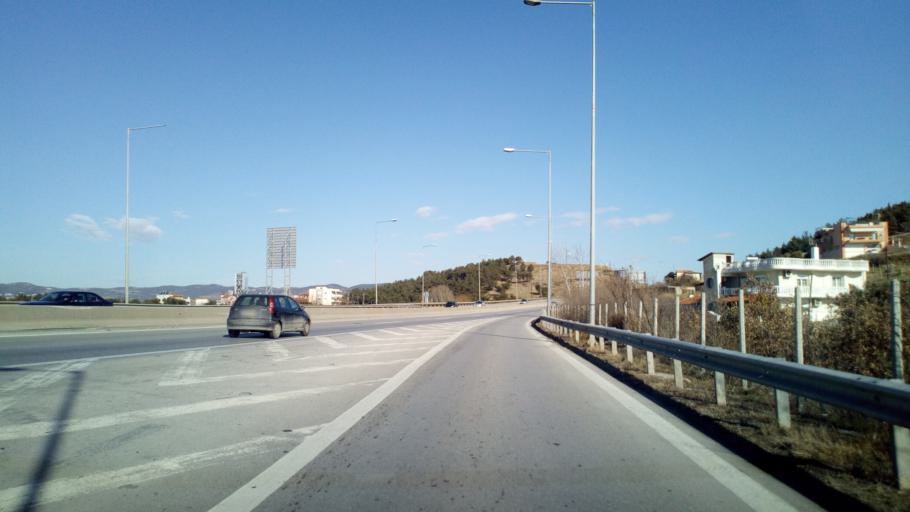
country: GR
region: Central Macedonia
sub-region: Nomos Thessalonikis
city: Efkarpia
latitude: 40.6835
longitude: 22.9574
